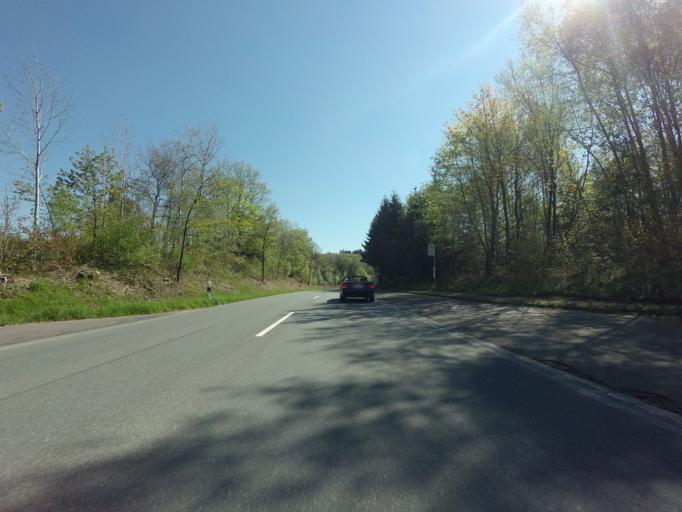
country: DE
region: North Rhine-Westphalia
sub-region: Regierungsbezirk Arnsberg
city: Attendorn
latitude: 51.1164
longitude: 7.9275
